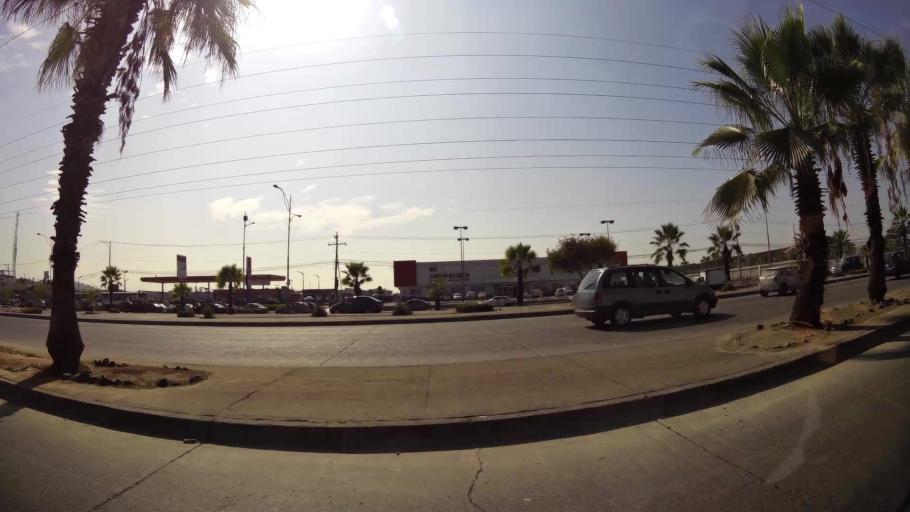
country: EC
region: Guayas
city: Eloy Alfaro
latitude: -2.0931
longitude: -79.9127
